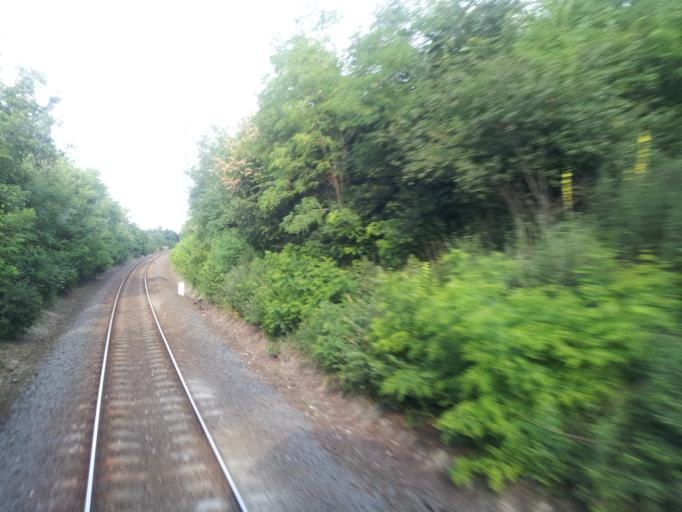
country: HU
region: Fejer
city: Szabadbattyan
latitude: 47.0823
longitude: 18.3592
